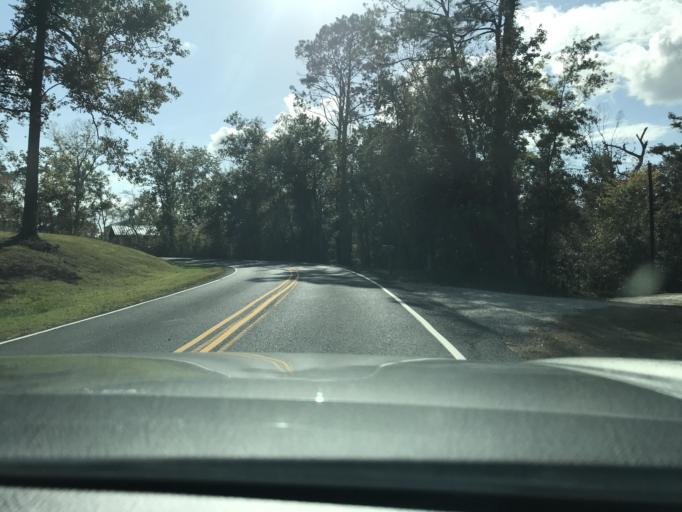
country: US
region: Louisiana
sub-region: Calcasieu Parish
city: Westlake
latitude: 30.3212
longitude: -93.2897
